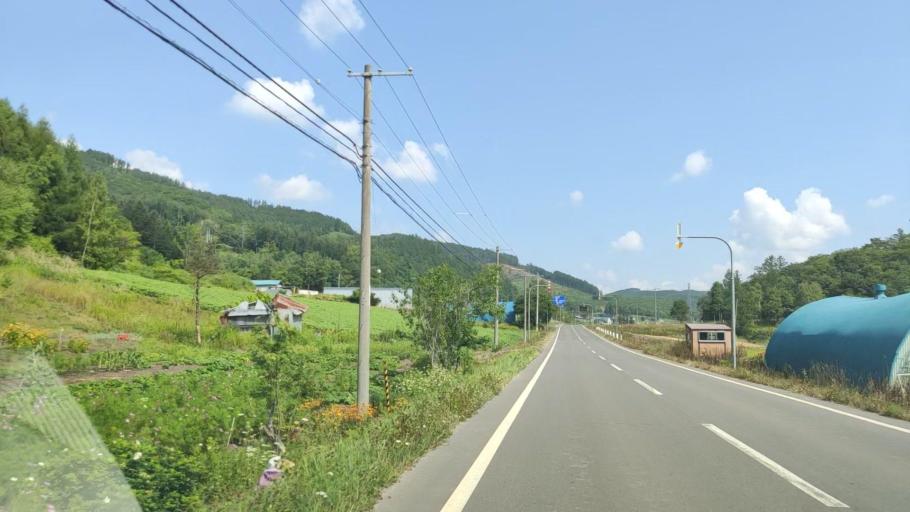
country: JP
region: Hokkaido
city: Shimo-furano
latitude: 43.4329
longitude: 142.4096
